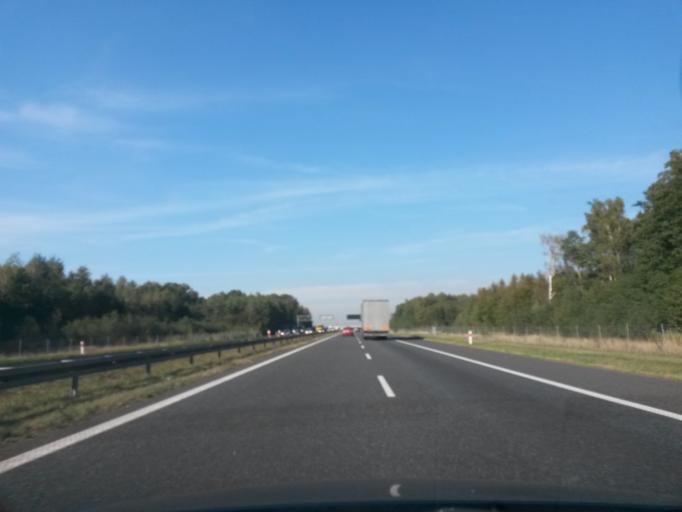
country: PL
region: Silesian Voivodeship
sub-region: Powiat gliwicki
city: Sosnicowice
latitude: 50.3319
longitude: 18.5458
